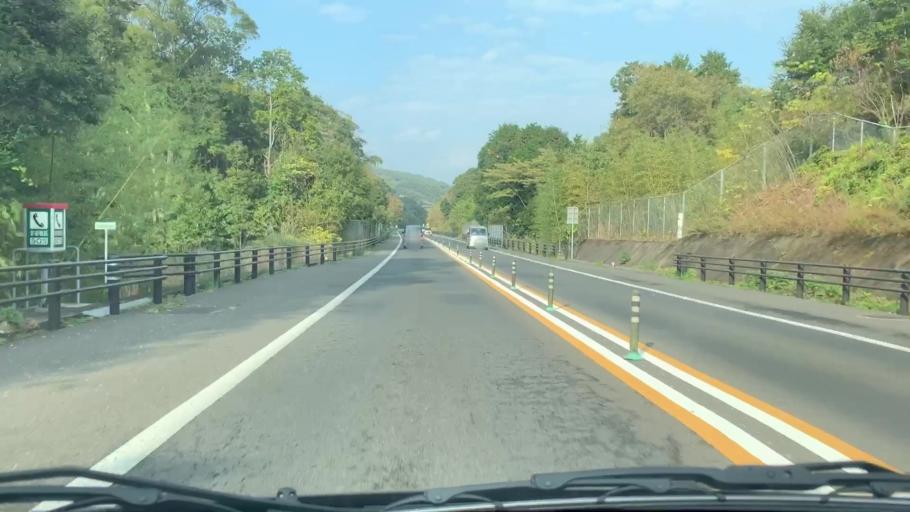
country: JP
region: Nagasaki
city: Sasebo
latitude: 33.0130
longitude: 129.7302
